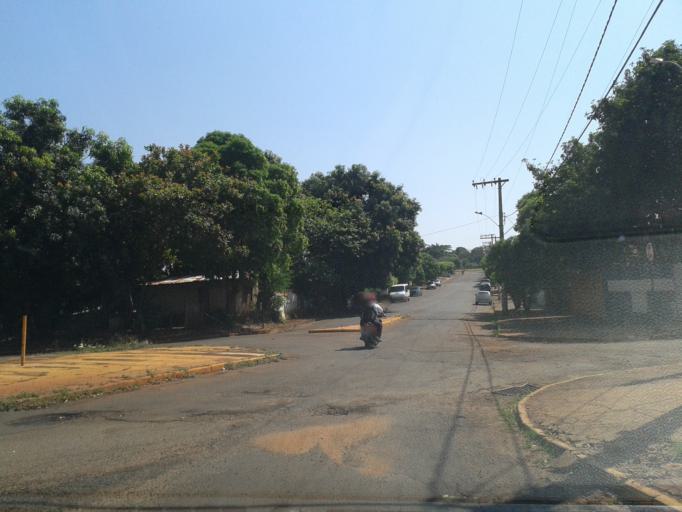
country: BR
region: Minas Gerais
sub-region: Ituiutaba
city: Ituiutaba
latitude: -18.9577
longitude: -49.4514
